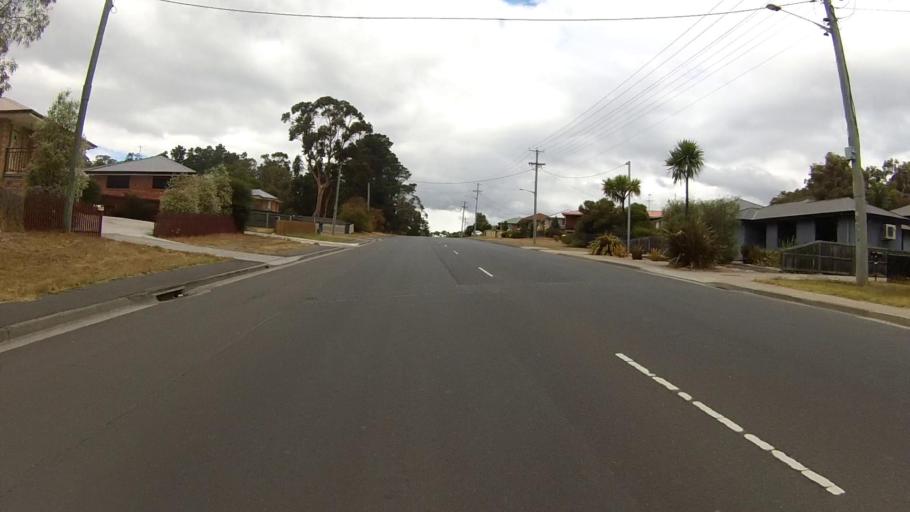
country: AU
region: Tasmania
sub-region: Glenorchy
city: Austins Ferry
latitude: -42.7690
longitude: 147.2456
